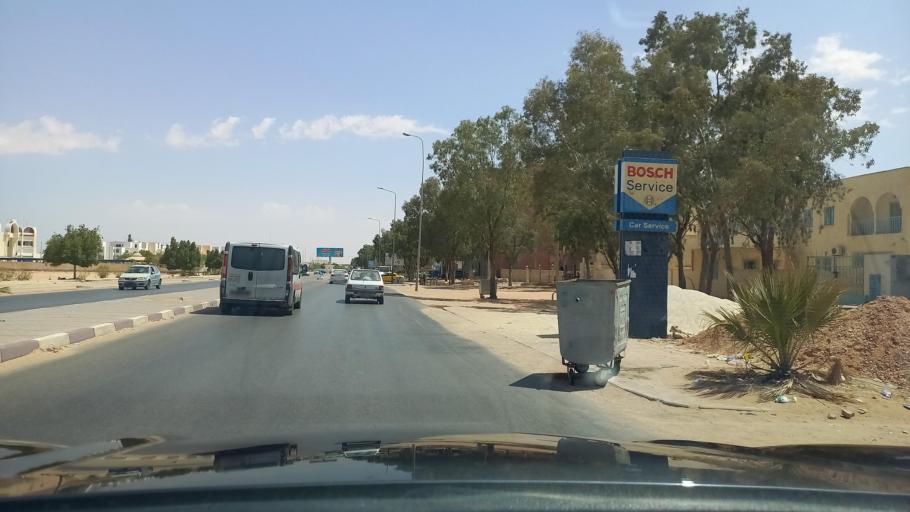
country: TN
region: Madanin
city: Medenine
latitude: 33.3613
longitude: 10.4665
